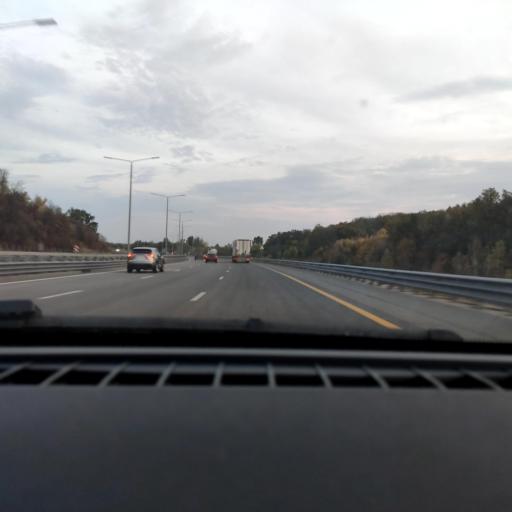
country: RU
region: Voronezj
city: Podgornoye
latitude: 51.8002
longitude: 39.2550
